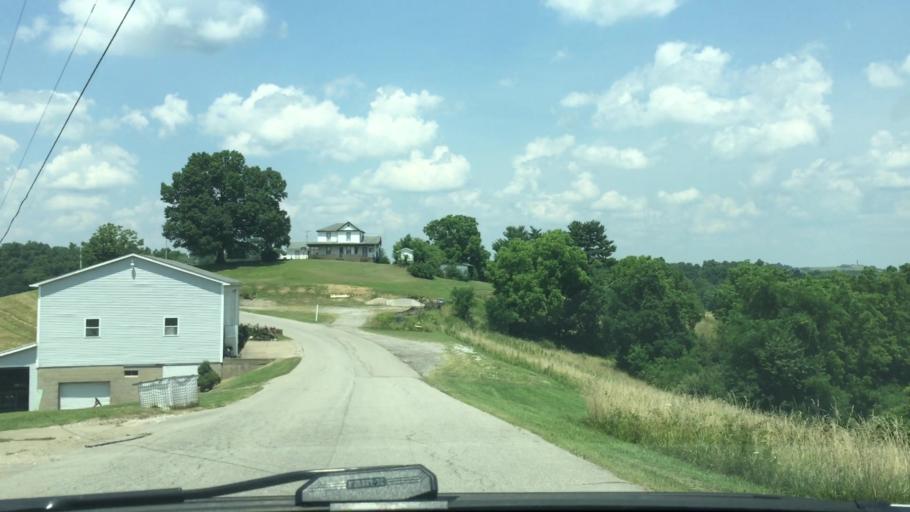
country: US
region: West Virginia
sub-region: Wetzel County
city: New Martinsville
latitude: 39.7053
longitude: -80.7447
